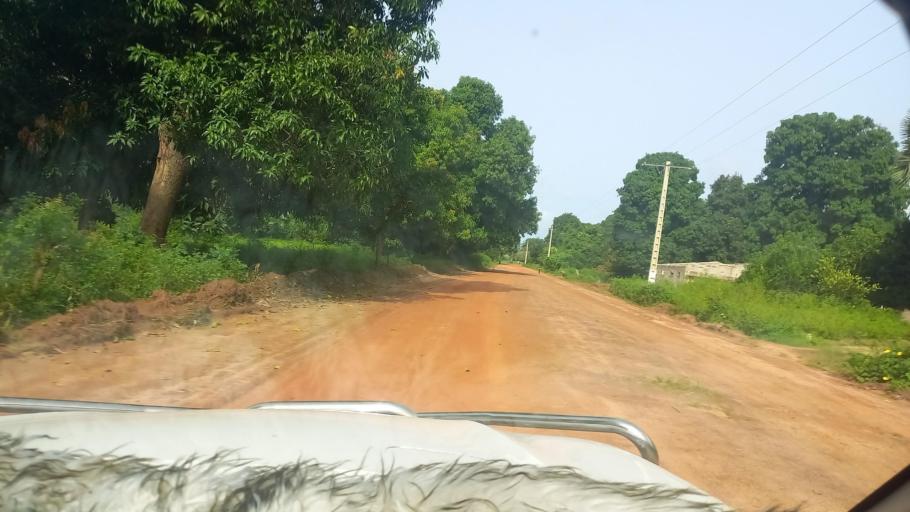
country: SN
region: Ziguinchor
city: Ziguinchor
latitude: 12.6702
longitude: -16.2736
